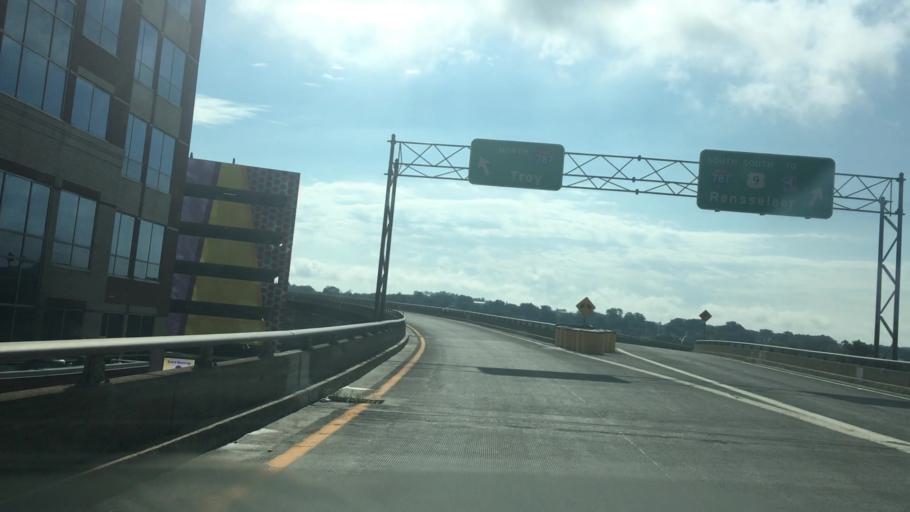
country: US
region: New York
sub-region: Albany County
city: Albany
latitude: 42.6532
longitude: -73.7489
